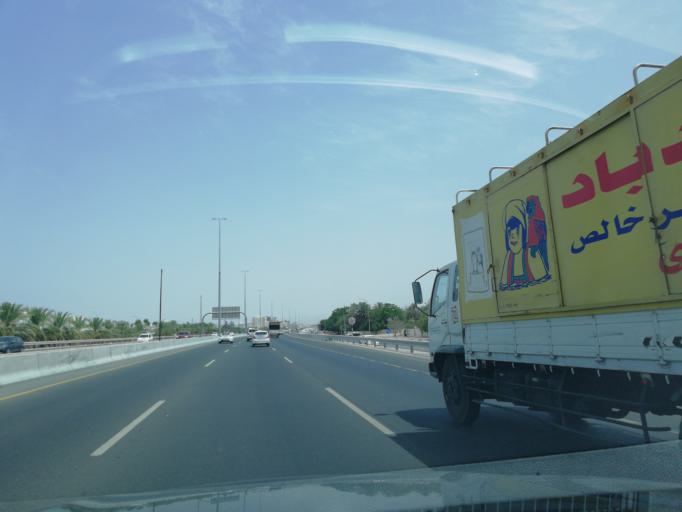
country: OM
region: Muhafazat Masqat
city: As Sib al Jadidah
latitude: 23.6483
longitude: 58.2176
